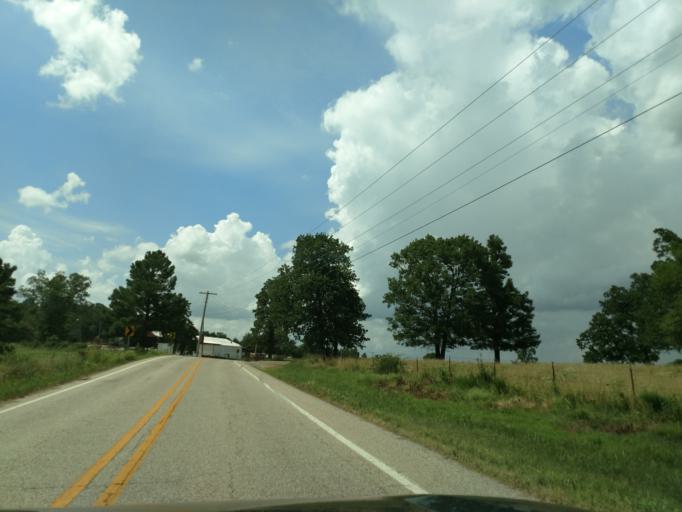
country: US
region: Arkansas
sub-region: Boone County
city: Harrison
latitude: 36.2661
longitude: -93.2310
